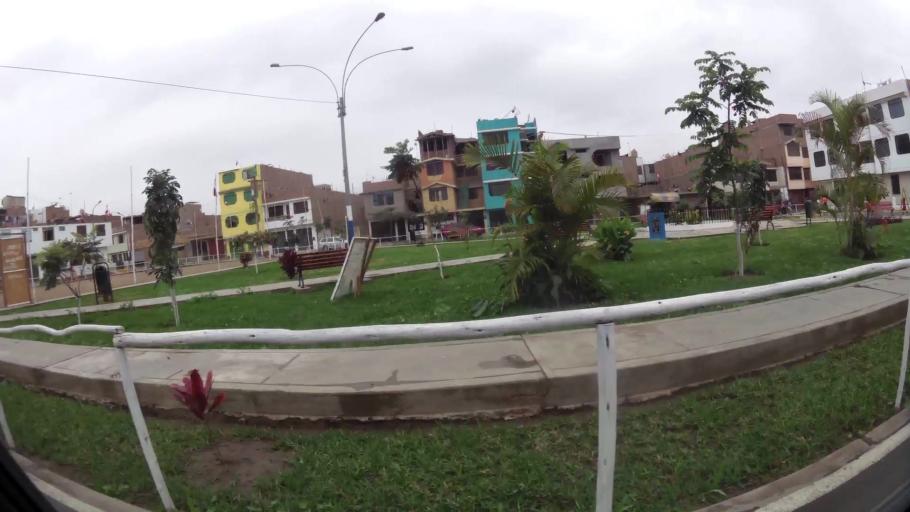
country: PE
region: Lima
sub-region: Lima
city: Independencia
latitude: -11.9666
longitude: -77.0923
